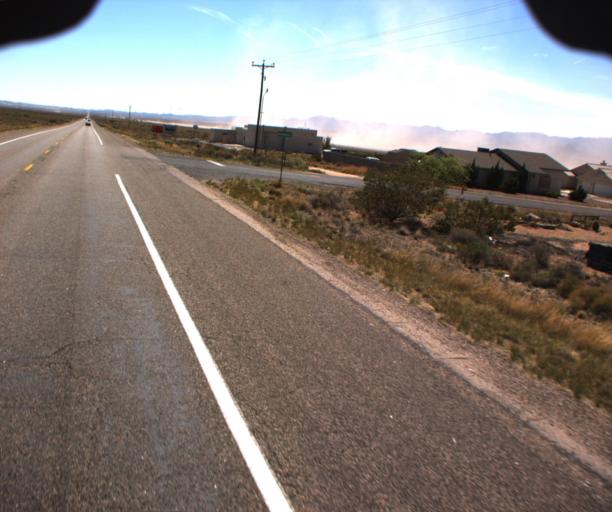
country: US
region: Arizona
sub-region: Mohave County
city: New Kingman-Butler
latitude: 35.3773
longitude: -113.8574
